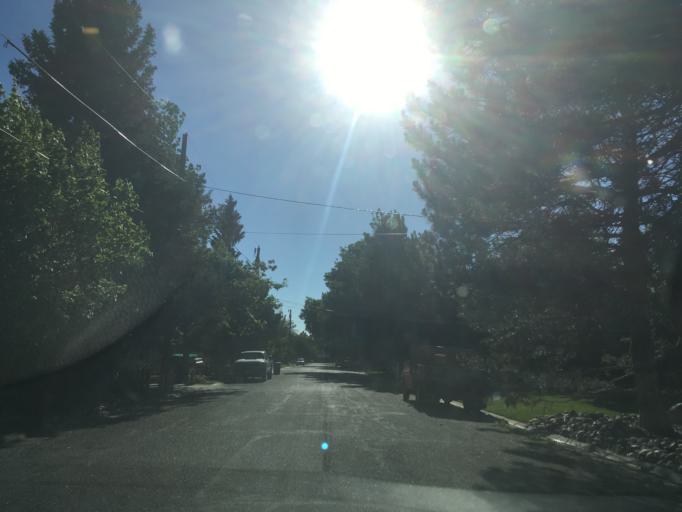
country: US
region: Montana
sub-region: Yellowstone County
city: Billings
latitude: 45.7938
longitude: -108.5601
